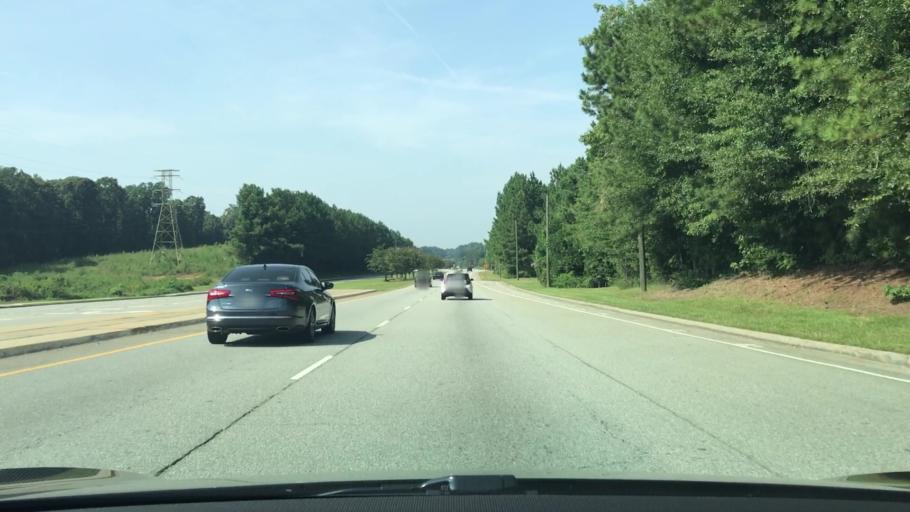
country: US
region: Georgia
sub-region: Gwinnett County
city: Sugar Hill
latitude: 34.1026
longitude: -84.0335
